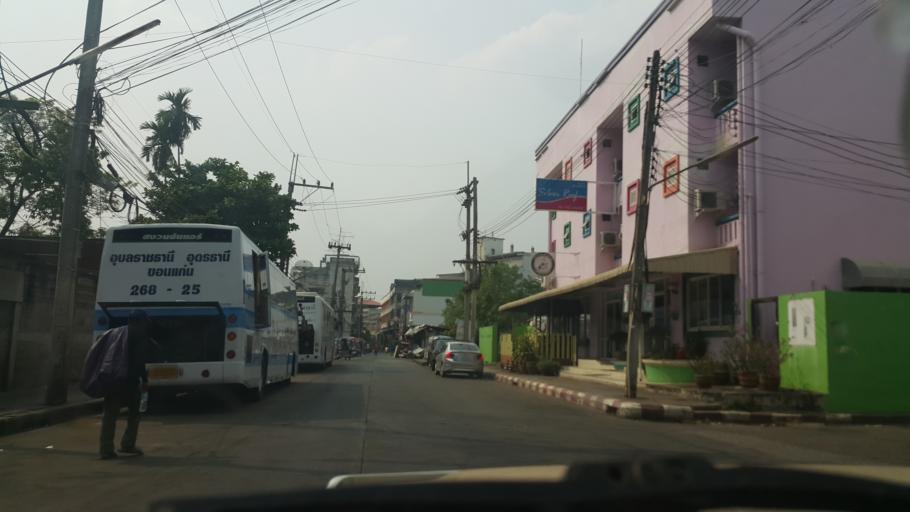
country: TH
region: Changwat Udon Thani
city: Udon Thani
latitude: 17.4030
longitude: 102.8013
